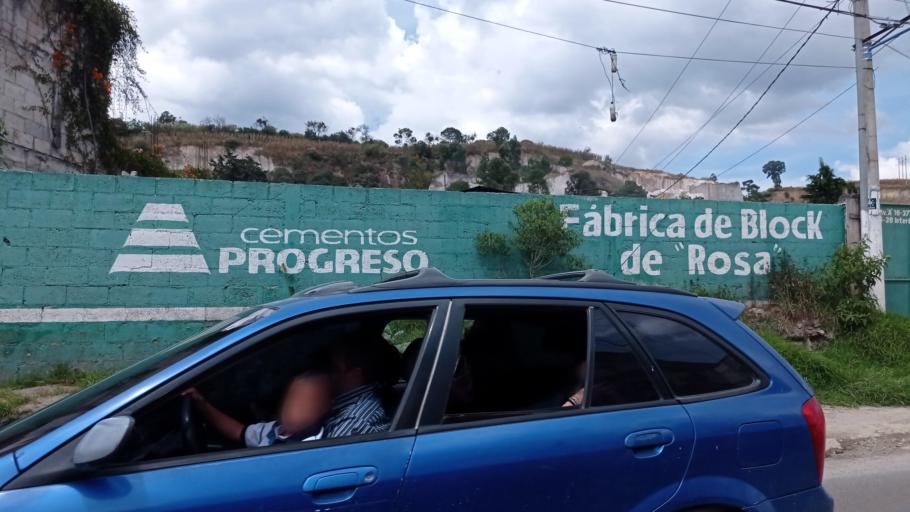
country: GT
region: Quetzaltenango
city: Quetzaltenango
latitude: 14.8518
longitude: -91.4964
